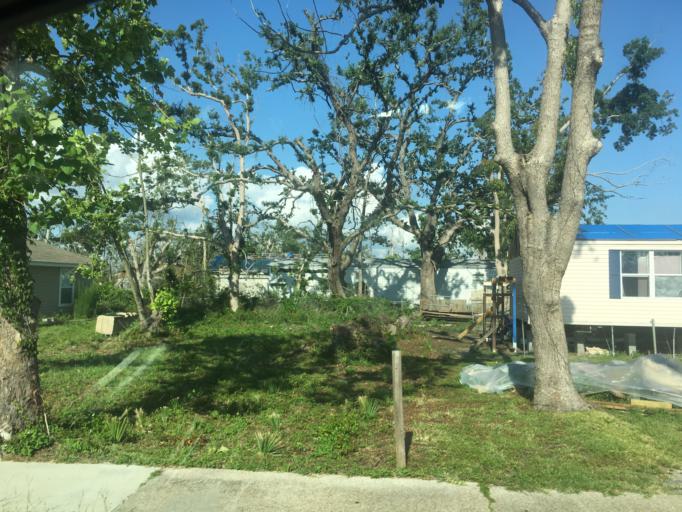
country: US
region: Florida
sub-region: Bay County
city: Springfield
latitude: 30.1607
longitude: -85.6165
